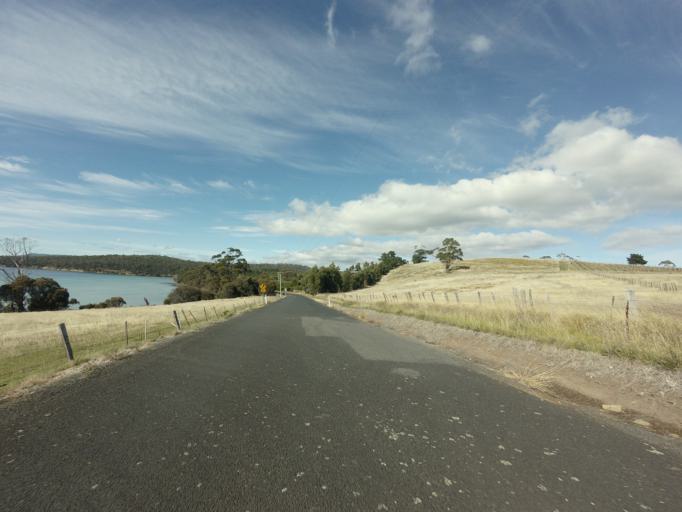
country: AU
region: Tasmania
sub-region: Clarence
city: Sandford
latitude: -43.0163
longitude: 147.7206
